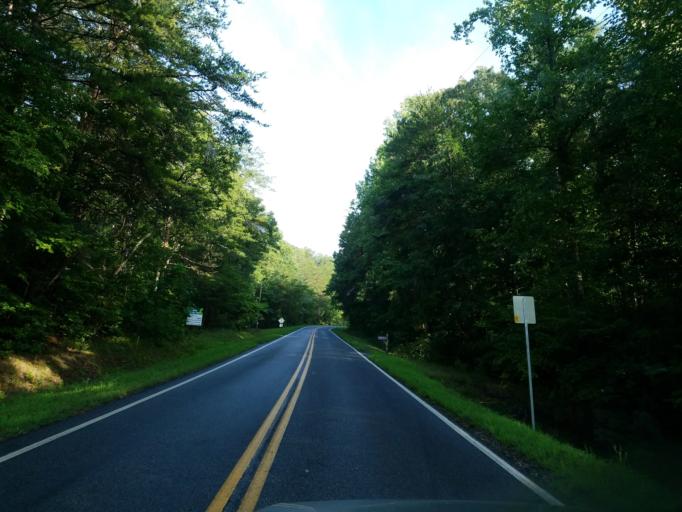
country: US
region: Georgia
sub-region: Lumpkin County
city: Dahlonega
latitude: 34.5715
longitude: -83.8932
